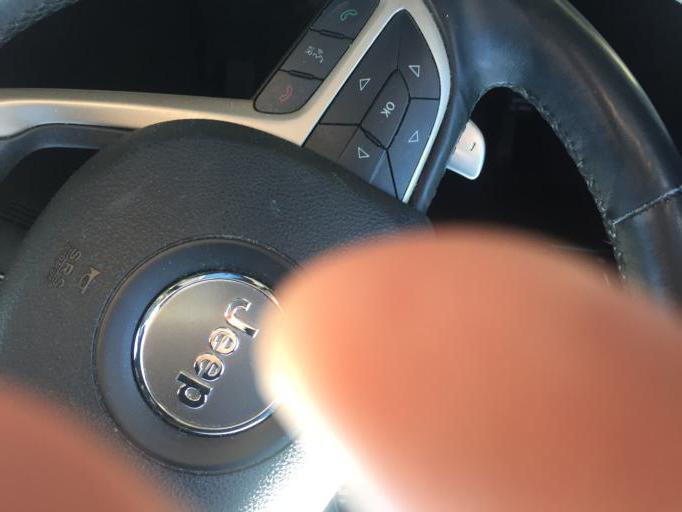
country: US
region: Massachusetts
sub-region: Plymouth County
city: North Plymouth
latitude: 41.9548
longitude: -70.6851
